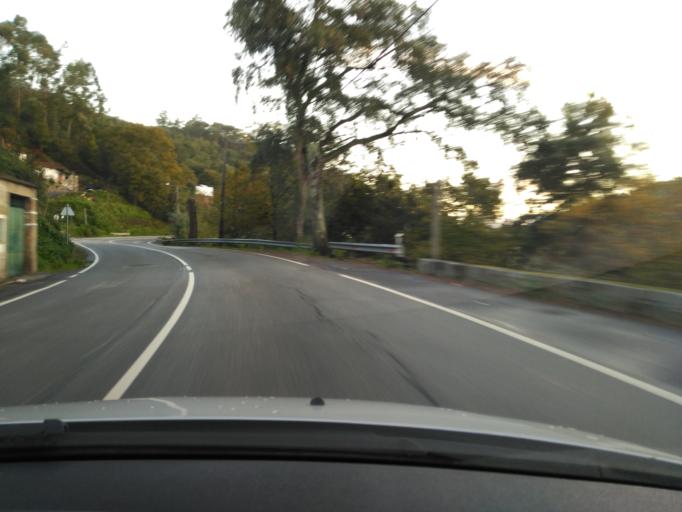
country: PT
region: Braga
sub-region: Braga
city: Braga
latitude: 41.5000
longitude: -8.4022
